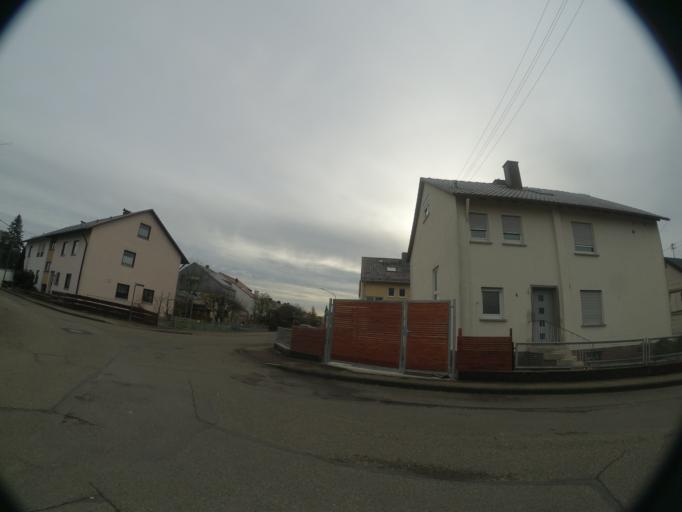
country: DE
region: Bavaria
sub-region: Swabia
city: Neu-Ulm
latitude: 48.4102
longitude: 10.0455
